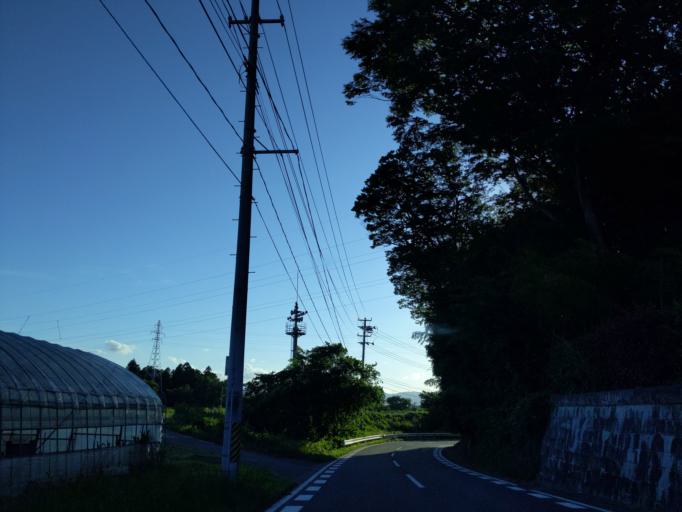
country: JP
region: Fukushima
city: Koriyama
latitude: 37.3886
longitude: 140.4133
